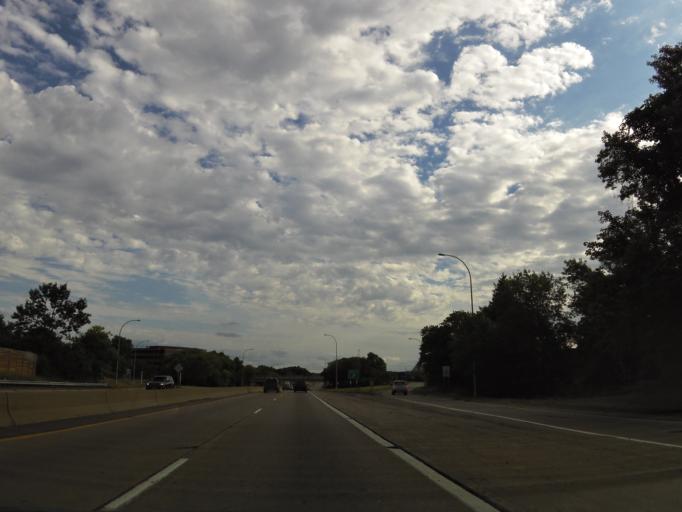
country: US
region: Minnesota
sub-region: Hennepin County
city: Minnetonka Mills
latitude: 44.9160
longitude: -93.4015
